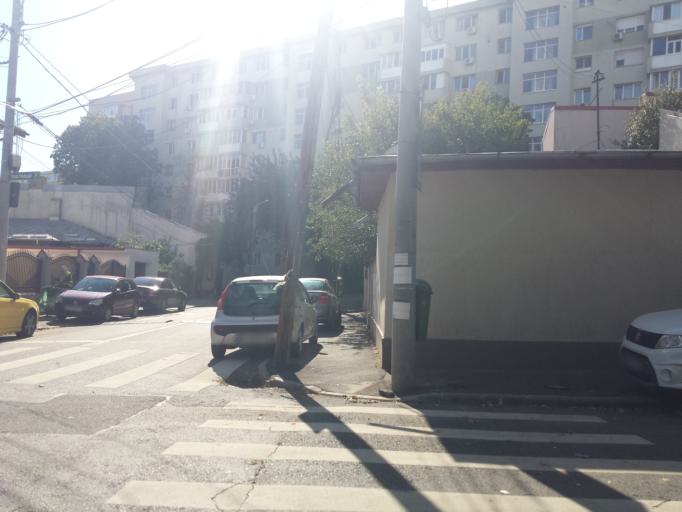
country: RO
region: Ilfov
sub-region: Comuna Chiajna
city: Rosu
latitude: 44.4620
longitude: 26.0594
